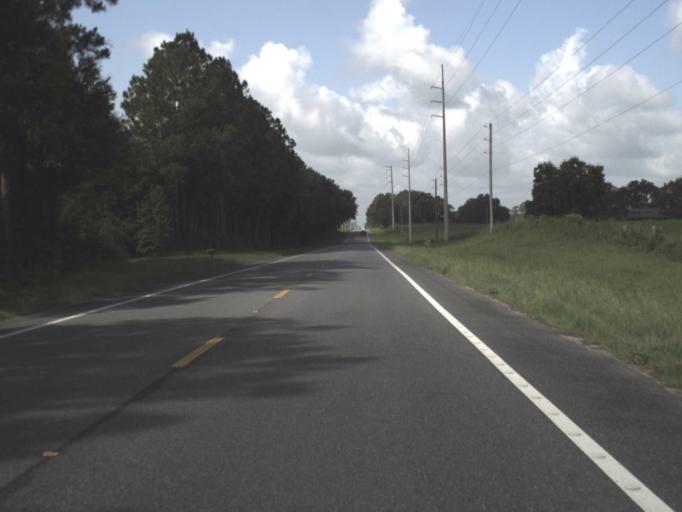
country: US
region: Florida
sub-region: Suwannee County
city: Wellborn
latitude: 30.0530
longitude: -82.7992
